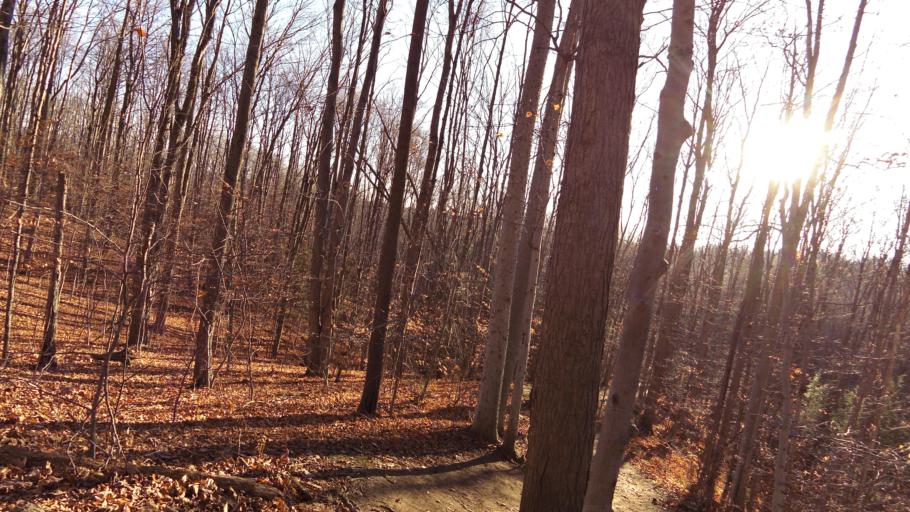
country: CA
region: Ontario
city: Orangeville
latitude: 43.9913
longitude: -80.0579
